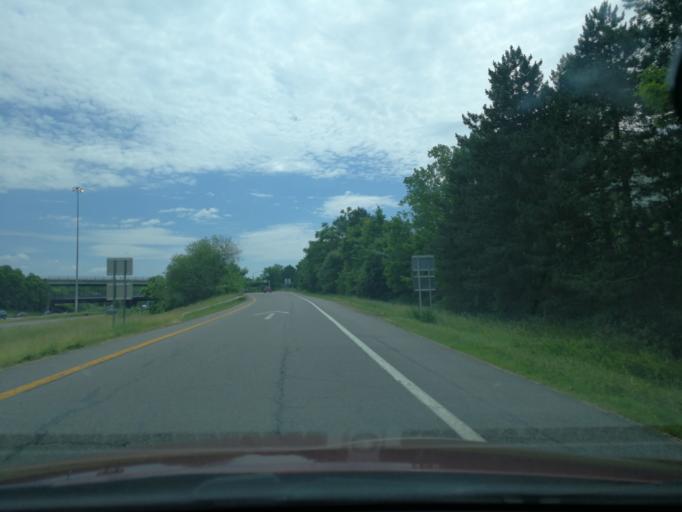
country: US
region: New York
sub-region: Monroe County
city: Greece
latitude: 43.2088
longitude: -77.6760
